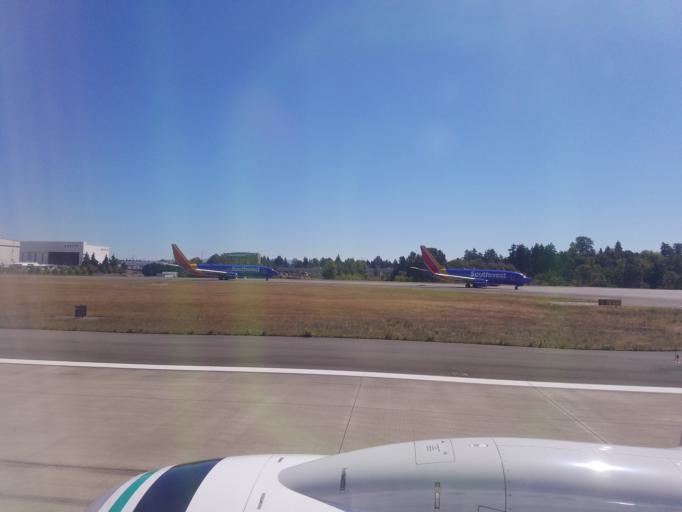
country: US
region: Washington
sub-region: King County
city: SeaTac
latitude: 47.4323
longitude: -122.3081
